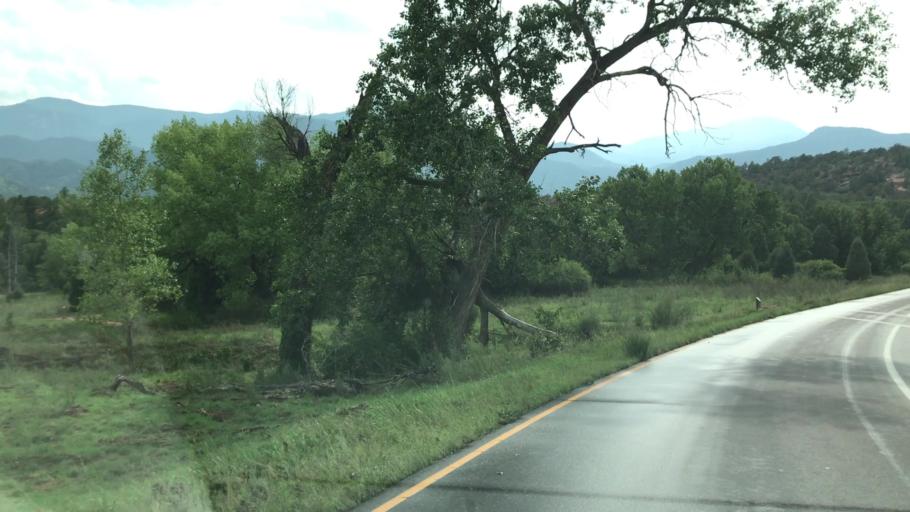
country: US
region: Colorado
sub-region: El Paso County
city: Manitou Springs
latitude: 38.8662
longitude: -104.8935
